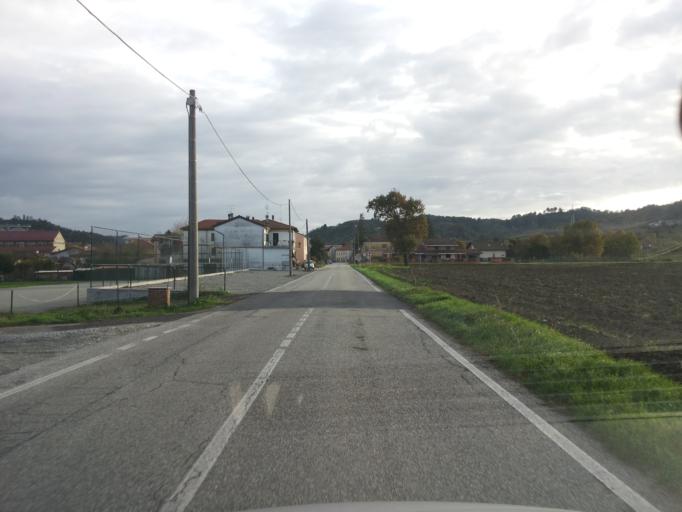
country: IT
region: Piedmont
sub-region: Provincia di Alessandria
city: Cereseto
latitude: 45.1056
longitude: 8.3077
